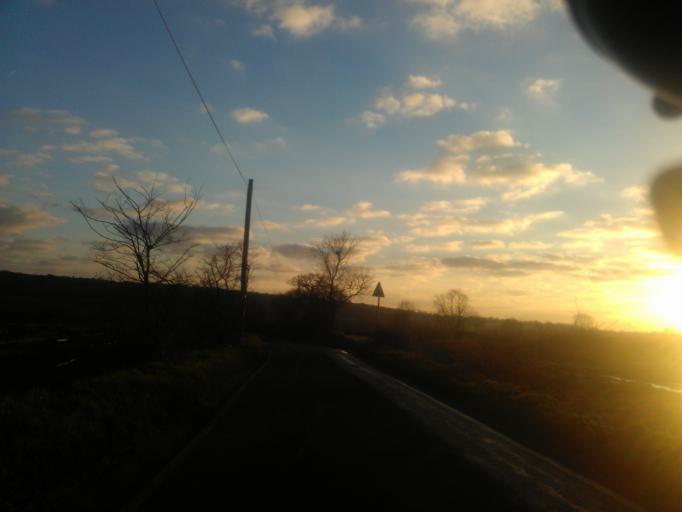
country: GB
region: England
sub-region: Essex
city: Hatfield Peverel
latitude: 51.7579
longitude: 0.5728
